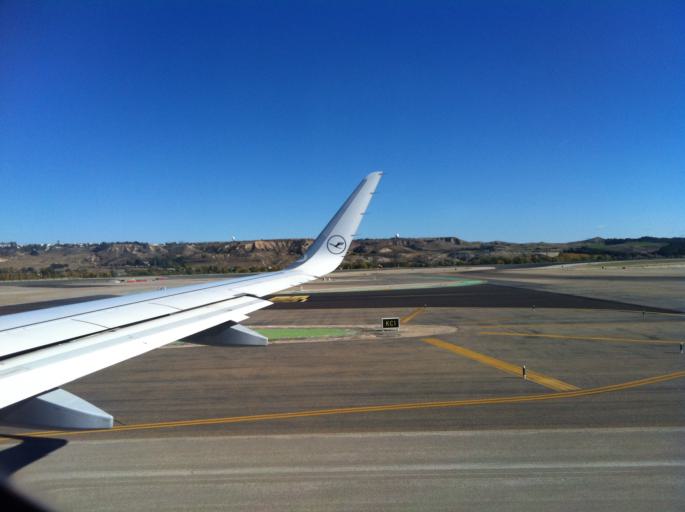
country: ES
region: Madrid
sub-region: Provincia de Madrid
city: Barajas de Madrid
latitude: 40.4934
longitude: -3.5625
